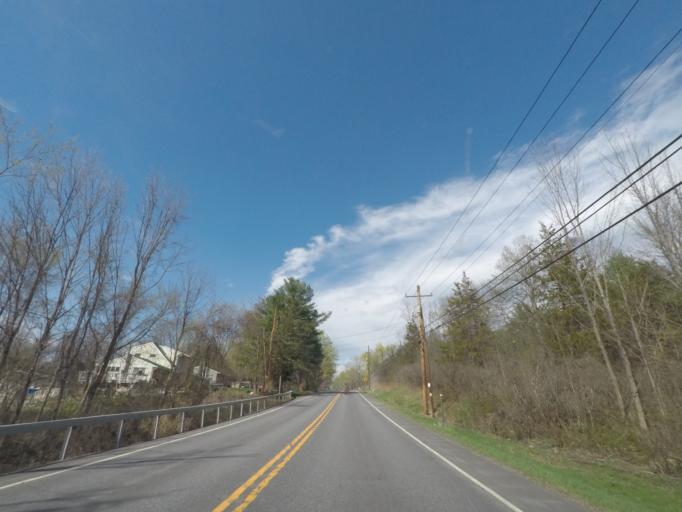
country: US
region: New York
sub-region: Greene County
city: Cairo
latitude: 42.3805
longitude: -74.0338
